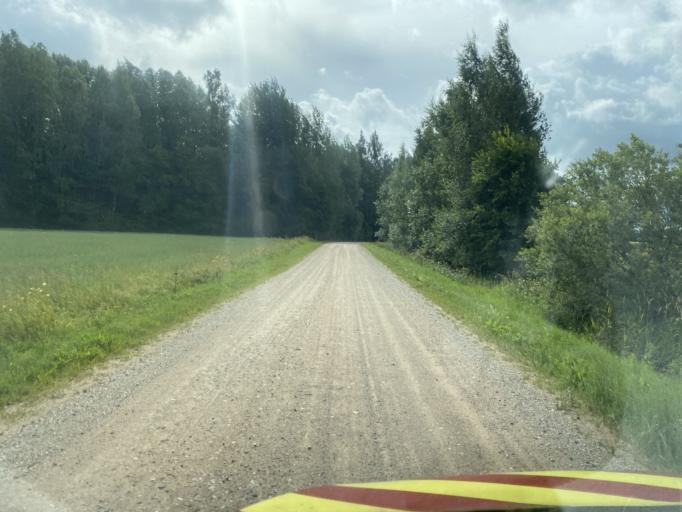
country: EE
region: Viljandimaa
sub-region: Karksi vald
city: Karksi-Nuia
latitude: 58.0794
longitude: 25.5184
